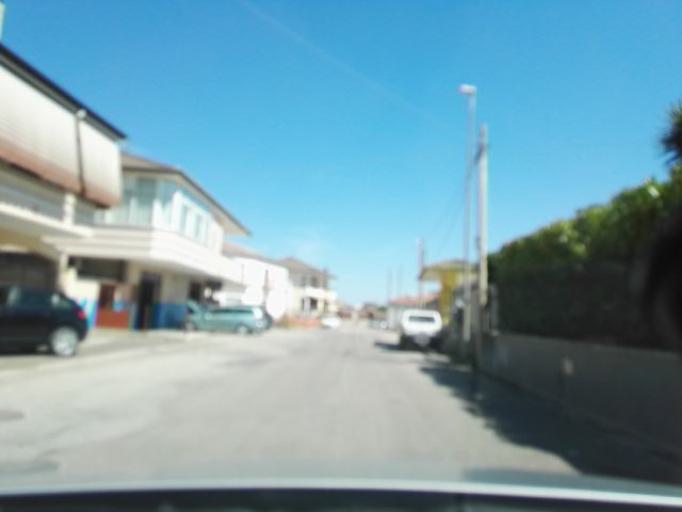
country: IT
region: Campania
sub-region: Provincia di Caserta
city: Casapesenna
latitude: 40.9894
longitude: 14.1300
